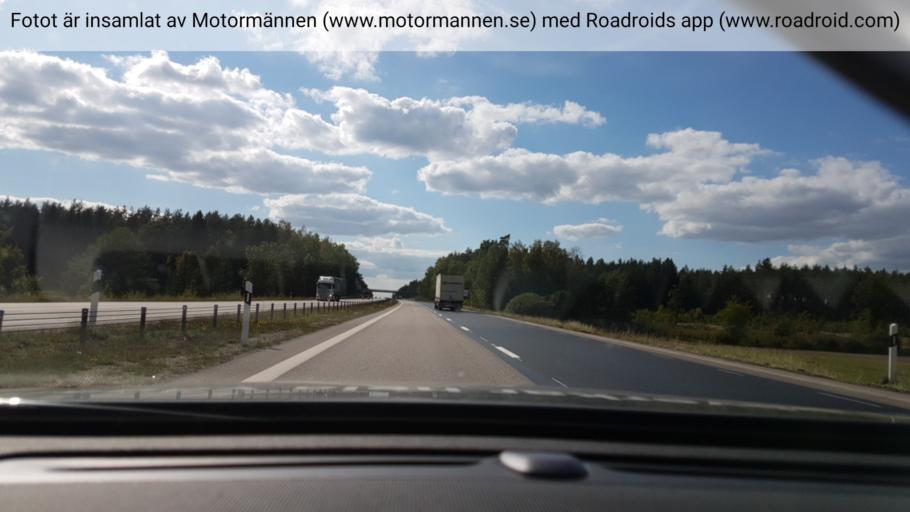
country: SE
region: OEstergoetland
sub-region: Linkopings Kommun
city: Vikingstad
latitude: 58.3840
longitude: 15.3659
